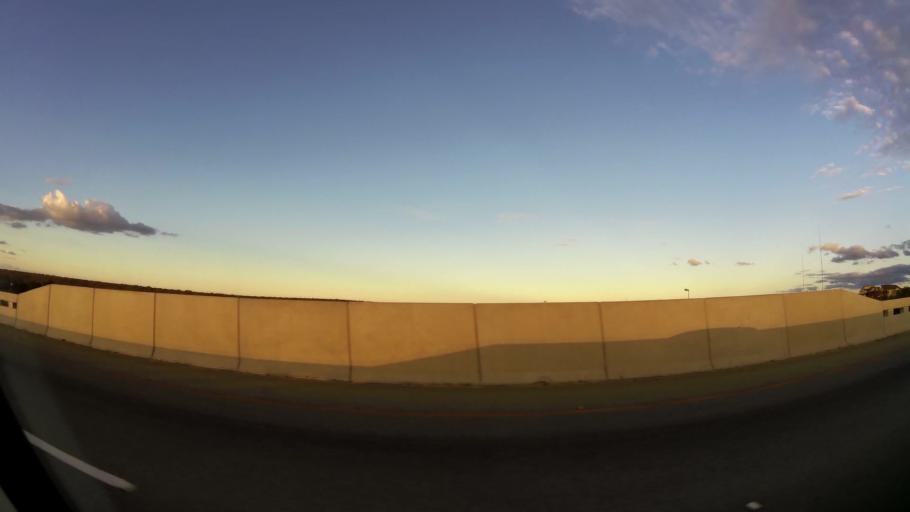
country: ZA
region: Limpopo
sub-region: Capricorn District Municipality
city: Polokwane
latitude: -23.8580
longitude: 29.5059
